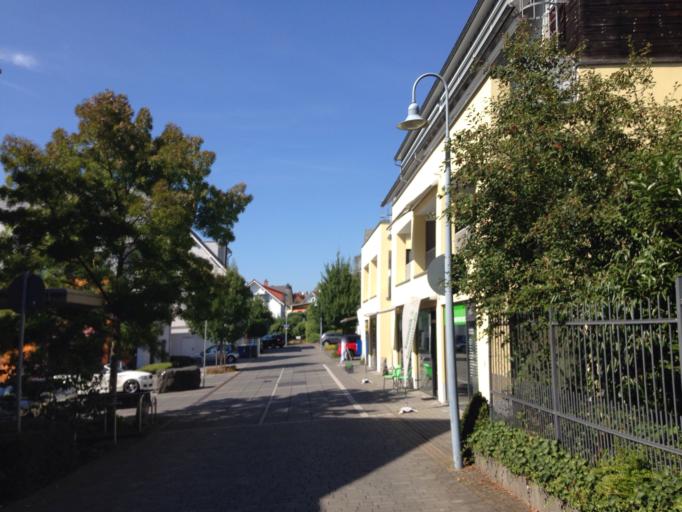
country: DE
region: Hesse
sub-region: Regierungsbezirk Giessen
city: Heuchelheim
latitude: 50.6167
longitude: 8.6031
